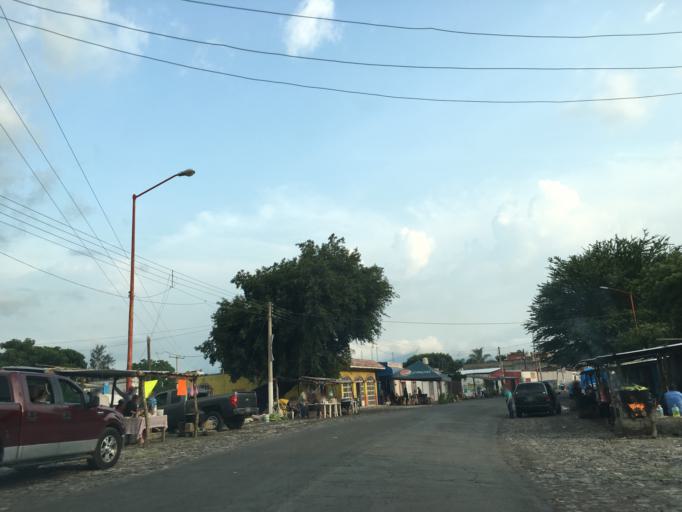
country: MX
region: Nayarit
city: Jala
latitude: 21.1006
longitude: -104.4322
